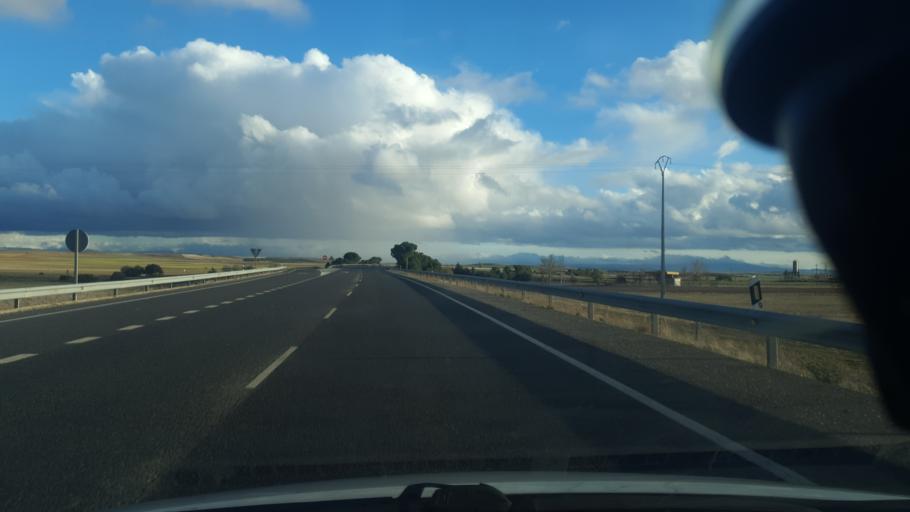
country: ES
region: Castille and Leon
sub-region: Provincia de Segovia
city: Codorniz
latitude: 41.0531
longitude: -4.6272
